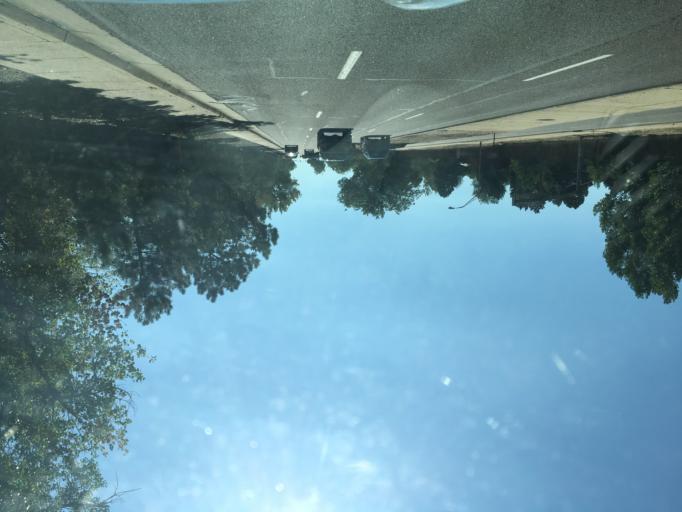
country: US
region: Colorado
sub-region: Arapahoe County
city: Dove Valley
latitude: 39.6313
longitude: -104.8067
